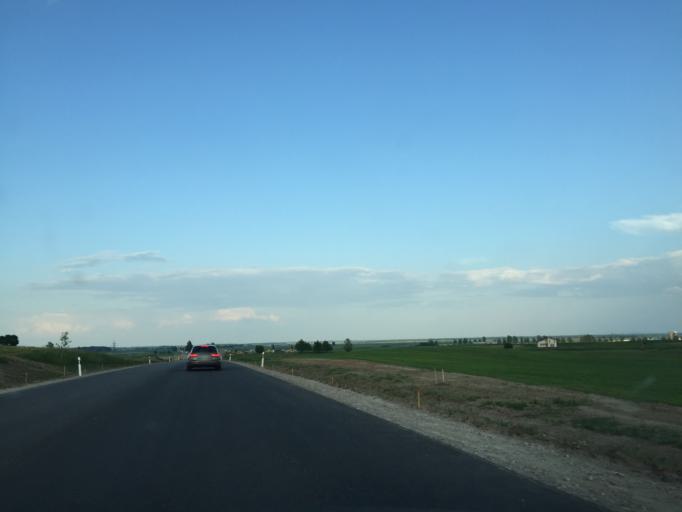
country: LT
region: Telsiu apskritis
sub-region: Telsiai
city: Telsiai
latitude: 56.0052
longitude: 22.2959
